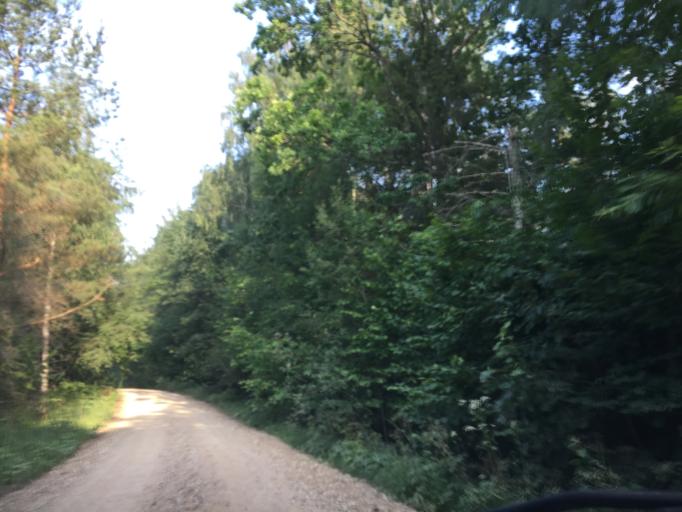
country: LT
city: Zagare
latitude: 56.4490
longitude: 23.1376
